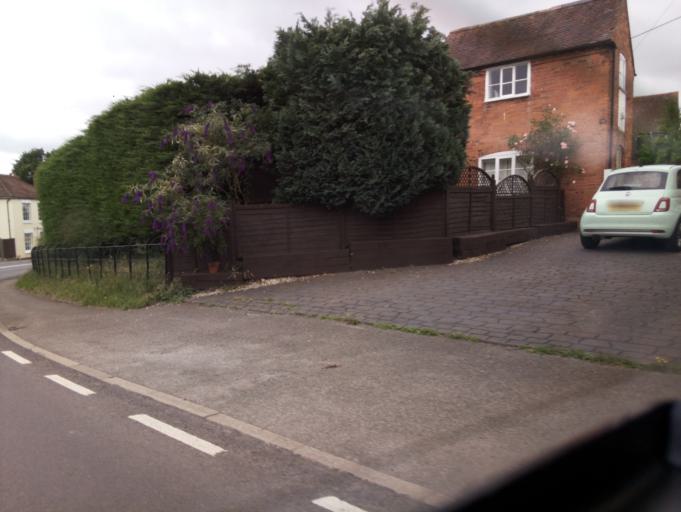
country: GB
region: England
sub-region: Worcestershire
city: Upton upon Severn
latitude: 52.0973
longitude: -2.2088
